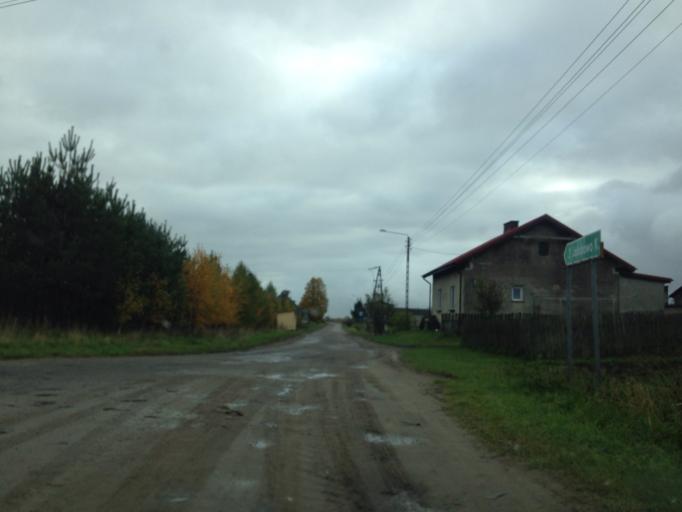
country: PL
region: Warmian-Masurian Voivodeship
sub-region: Powiat ilawski
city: Susz
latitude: 53.6579
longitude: 19.3346
